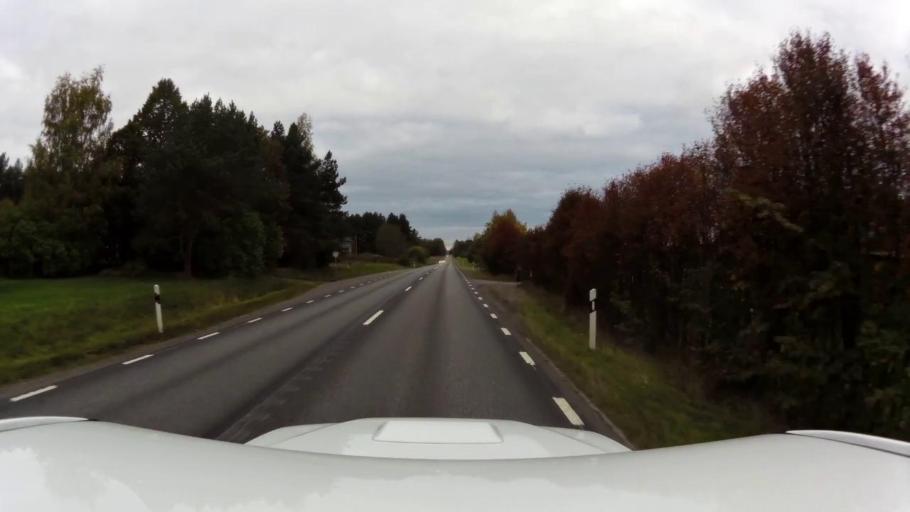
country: SE
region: OEstergoetland
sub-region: Linkopings Kommun
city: Ljungsbro
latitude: 58.5014
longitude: 15.4555
